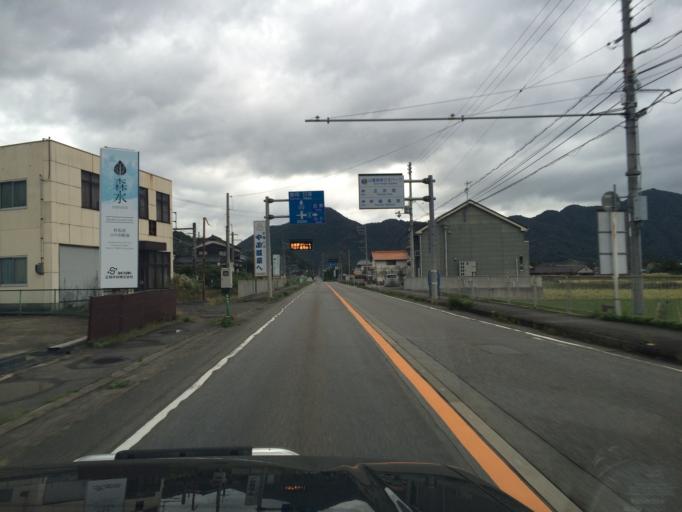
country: JP
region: Hyogo
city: Toyooka
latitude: 35.4218
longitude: 134.7905
